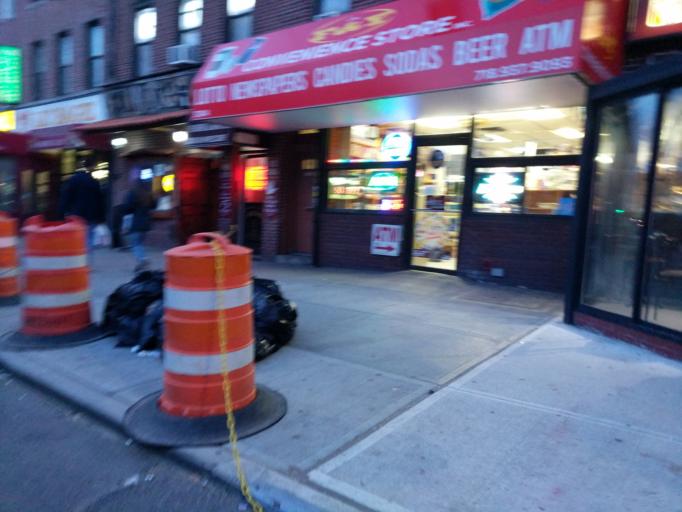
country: US
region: New York
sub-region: Queens County
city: Long Island City
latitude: 40.7565
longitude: -73.9296
